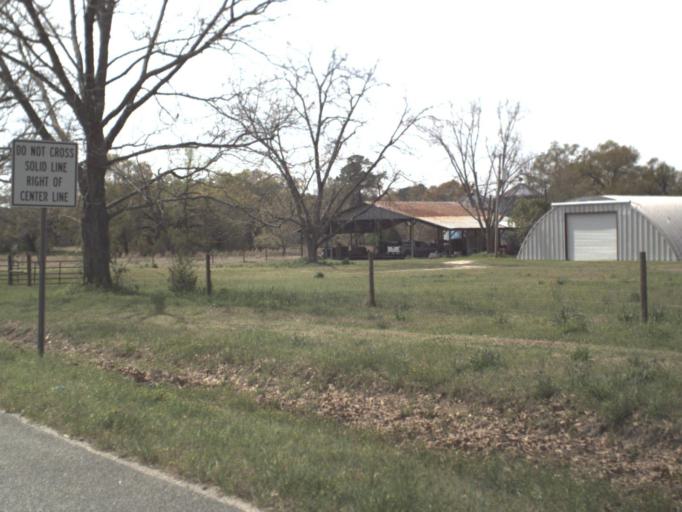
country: US
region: Florida
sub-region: Jackson County
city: Graceville
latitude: 30.9934
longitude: -85.4794
